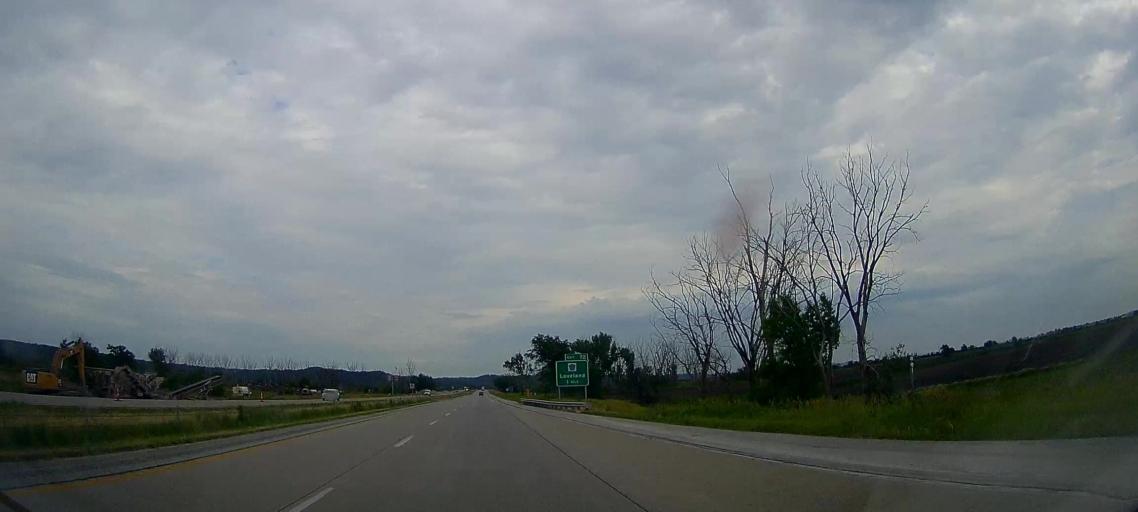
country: US
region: Iowa
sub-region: Harrison County
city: Missouri Valley
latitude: 41.5143
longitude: -95.9137
